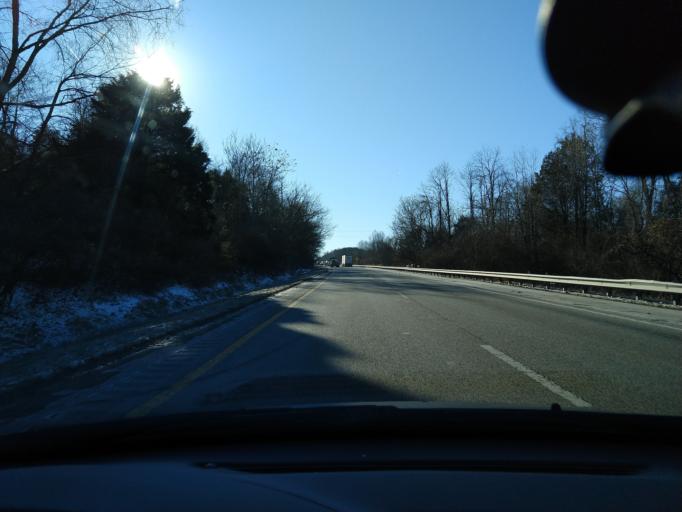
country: US
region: Virginia
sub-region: Botetourt County
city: Fincastle
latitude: 37.4570
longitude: -79.8402
